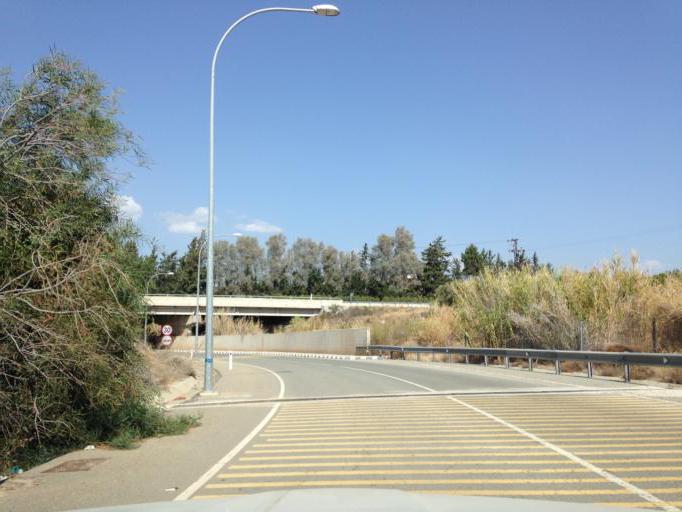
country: CY
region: Limassol
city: Pissouri
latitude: 34.7046
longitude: 32.5628
